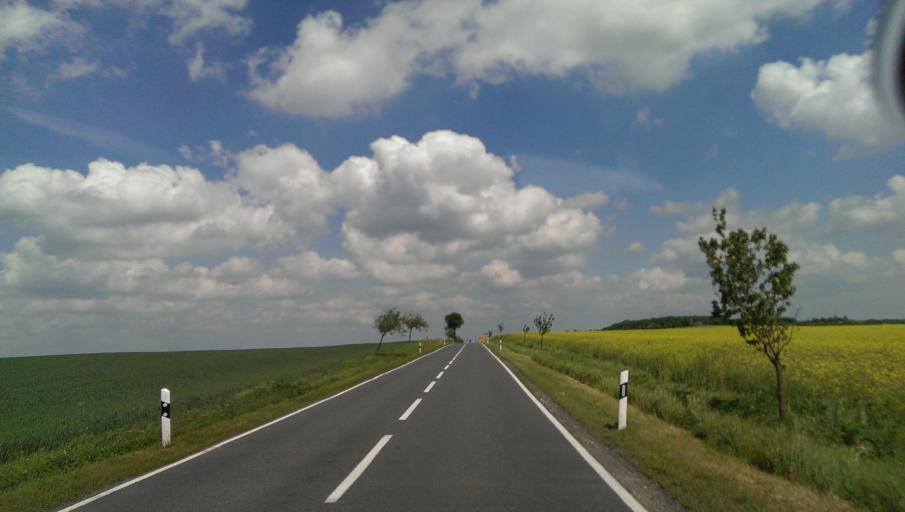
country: DE
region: Saxony-Anhalt
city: Biere
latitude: 51.9861
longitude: 11.6808
